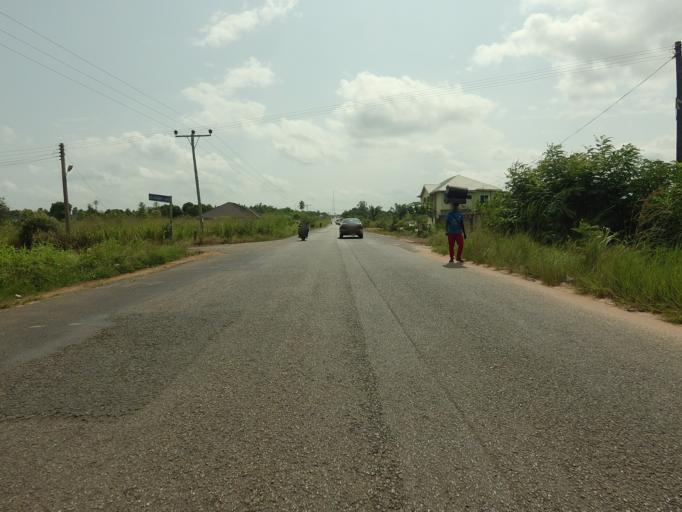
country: TG
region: Maritime
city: Lome
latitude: 6.2290
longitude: 1.0126
